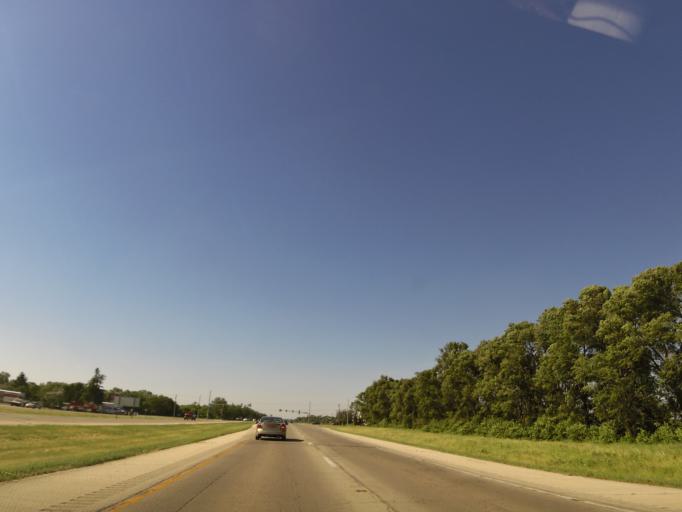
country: US
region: Illinois
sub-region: Winnebago County
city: South Beloit
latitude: 42.4687
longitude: -89.0194
